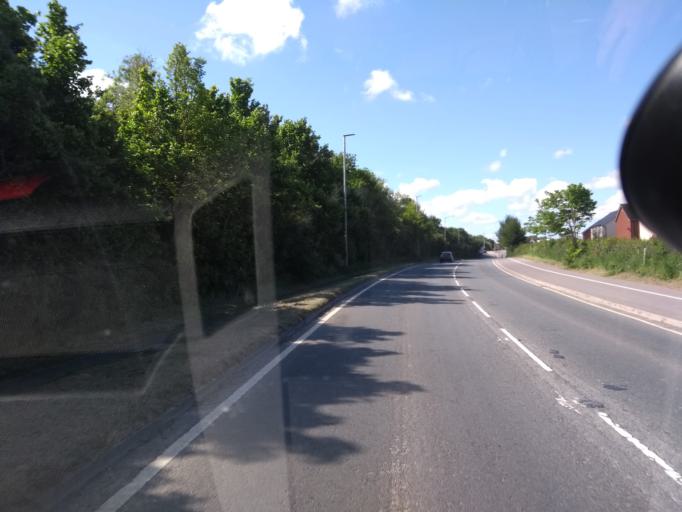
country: GB
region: England
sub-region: Somerset
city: Bridgwater
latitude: 51.1076
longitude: -2.9941
